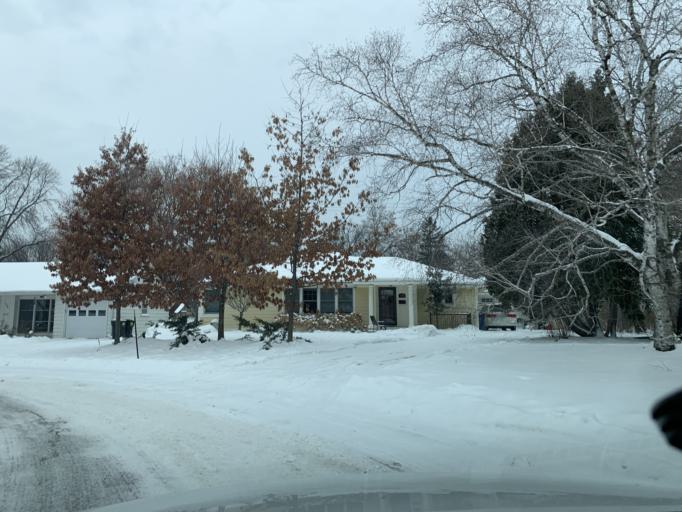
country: US
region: Minnesota
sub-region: Hennepin County
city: Edina
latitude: 44.9160
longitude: -93.3527
